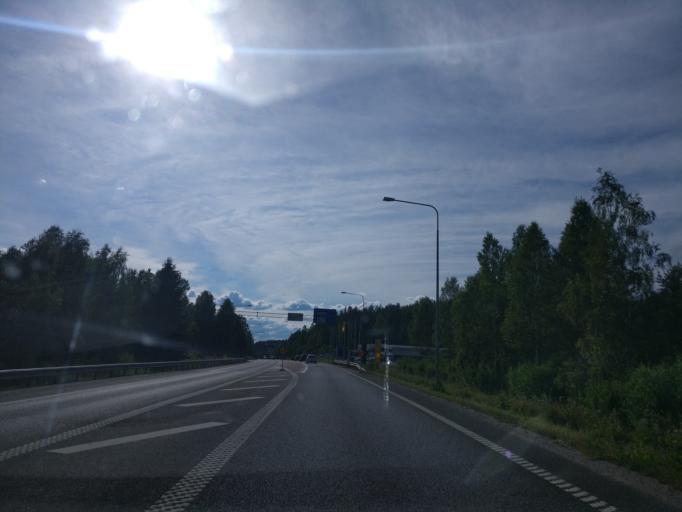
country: SE
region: Vaermland
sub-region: Arvika Kommun
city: Arvika
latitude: 59.6619
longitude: 12.6283
